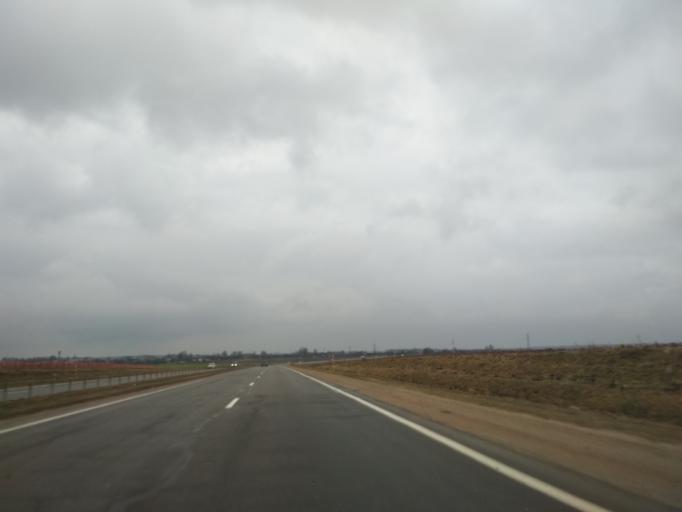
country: BY
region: Minsk
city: Dukora
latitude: 53.6794
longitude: 27.9241
